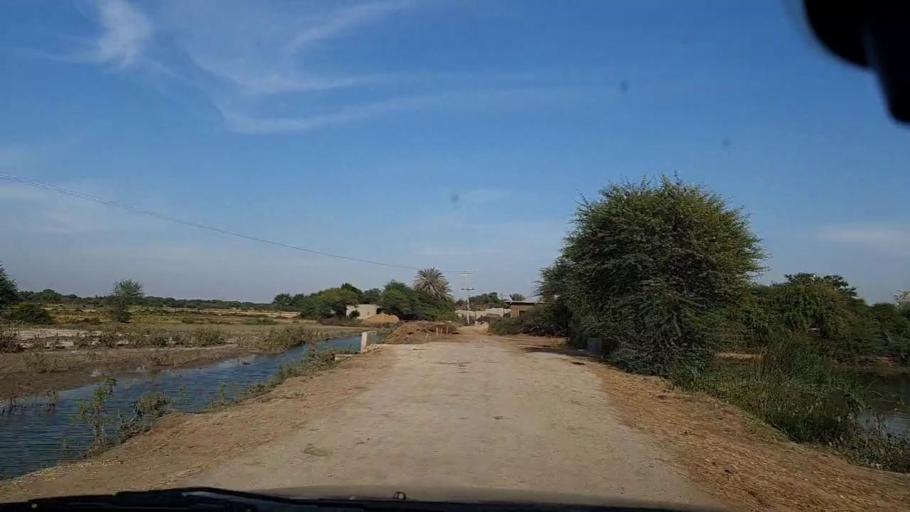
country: PK
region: Sindh
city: Mirpur Batoro
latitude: 24.6349
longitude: 68.3016
